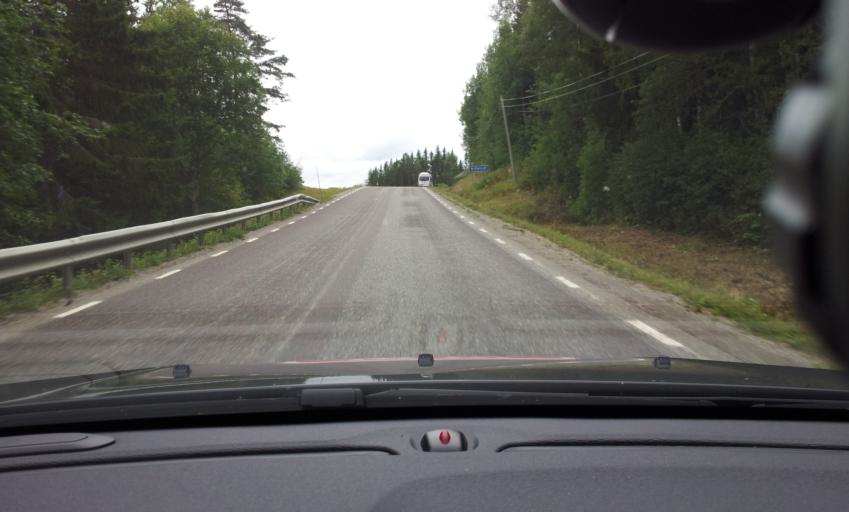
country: SE
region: Jaemtland
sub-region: Braecke Kommun
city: Braecke
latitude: 63.0220
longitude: 15.2309
